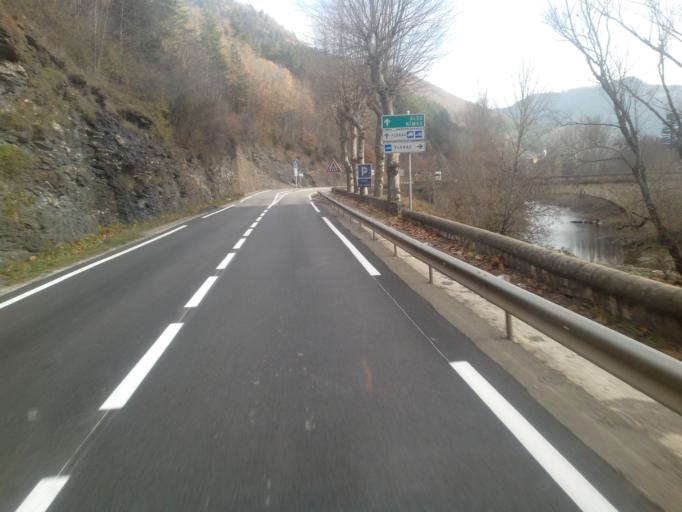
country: FR
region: Languedoc-Roussillon
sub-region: Departement de la Lozere
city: Florac
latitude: 44.3323
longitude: 3.5898
